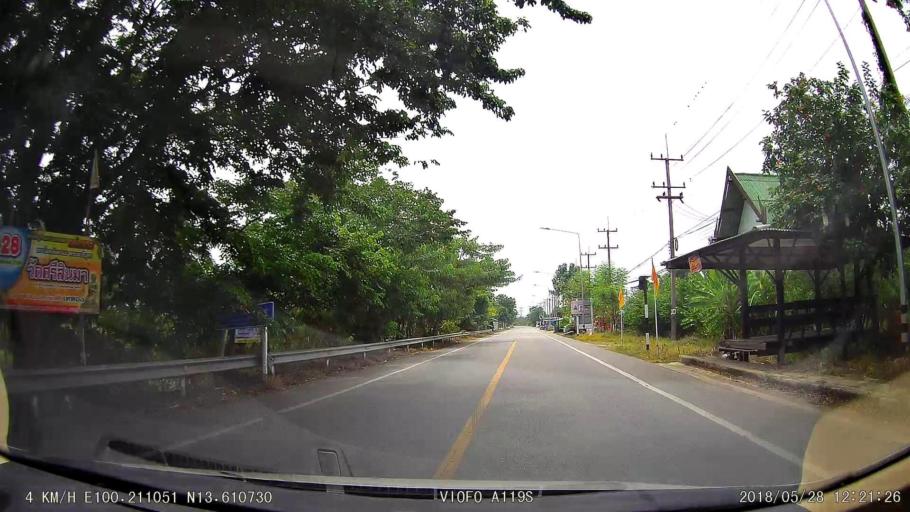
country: TH
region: Samut Sakhon
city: Krathum Baen
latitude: 13.6223
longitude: 100.2069
